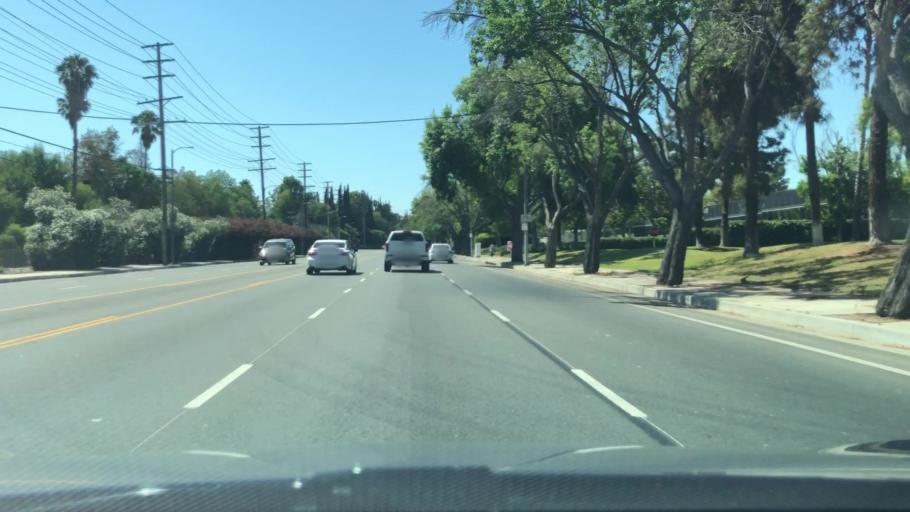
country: US
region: California
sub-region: Los Angeles County
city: Woodland Hills
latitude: 34.1767
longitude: -118.5896
